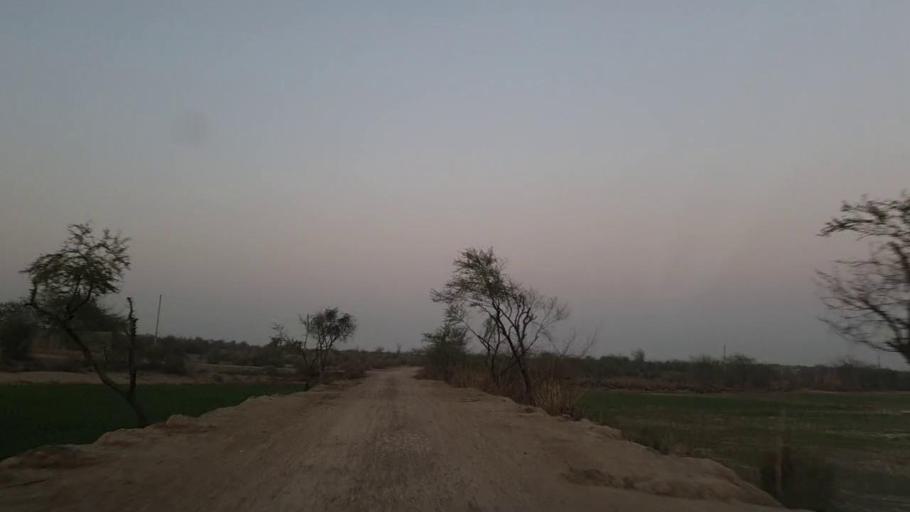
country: PK
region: Sindh
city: Bandhi
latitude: 26.6086
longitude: 68.3883
